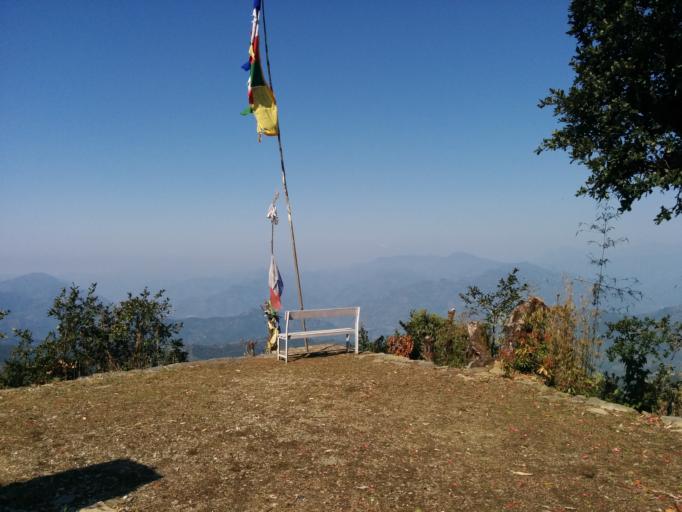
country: NP
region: Western Region
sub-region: Gandaki Zone
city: Pokhara
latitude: 28.2300
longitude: 83.7951
